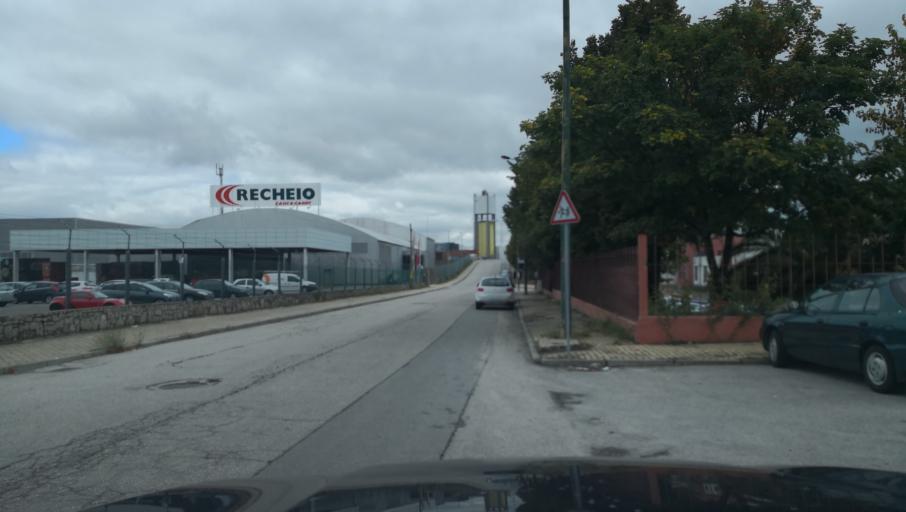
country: PT
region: Vila Real
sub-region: Vila Real
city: Vila Real
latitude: 41.2758
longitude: -7.7044
